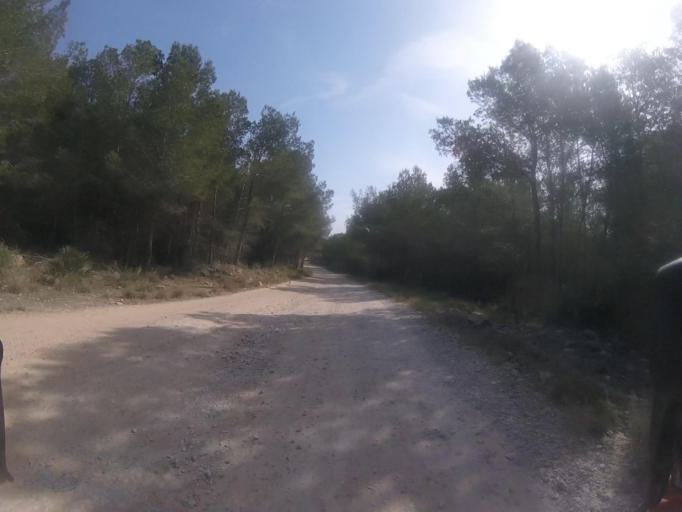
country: ES
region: Valencia
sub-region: Provincia de Castello
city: Alcoceber
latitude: 40.2731
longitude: 0.3087
